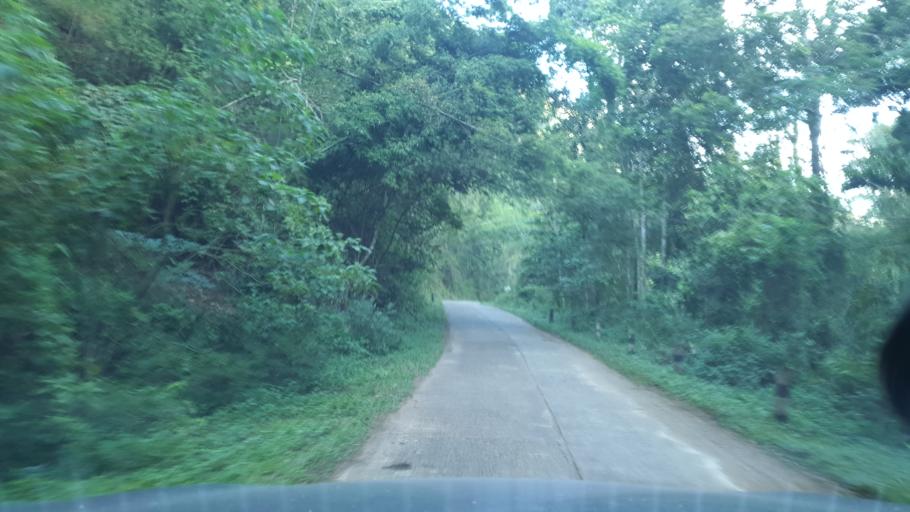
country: TH
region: Chiang Mai
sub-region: Amphoe Chiang Dao
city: Chiang Dao
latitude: 19.3891
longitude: 98.7692
